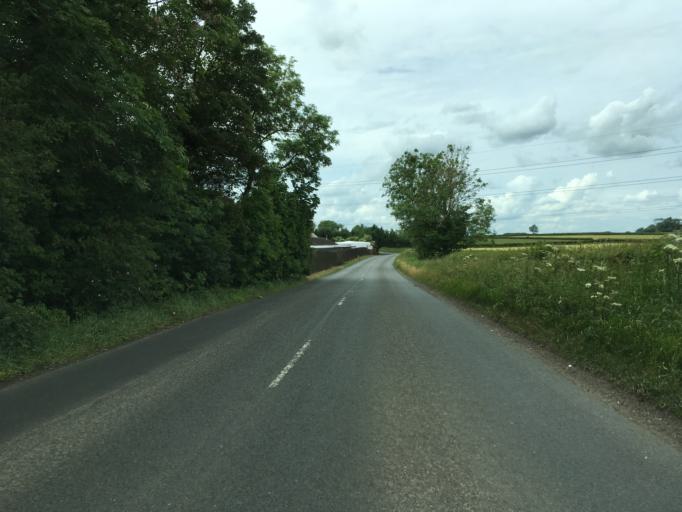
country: GB
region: England
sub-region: Wiltshire
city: Charlton
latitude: 51.5656
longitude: -2.0186
